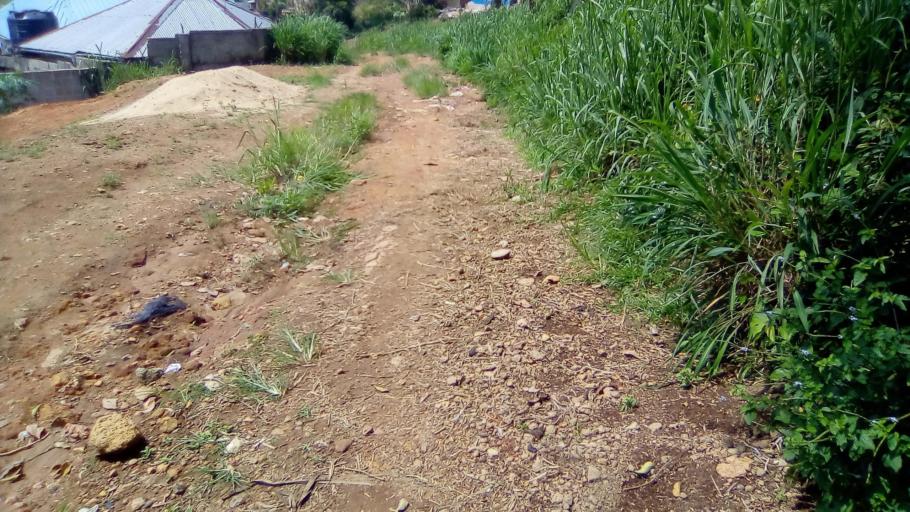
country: SL
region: Southern Province
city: Bo
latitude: 7.9746
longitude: -11.7440
